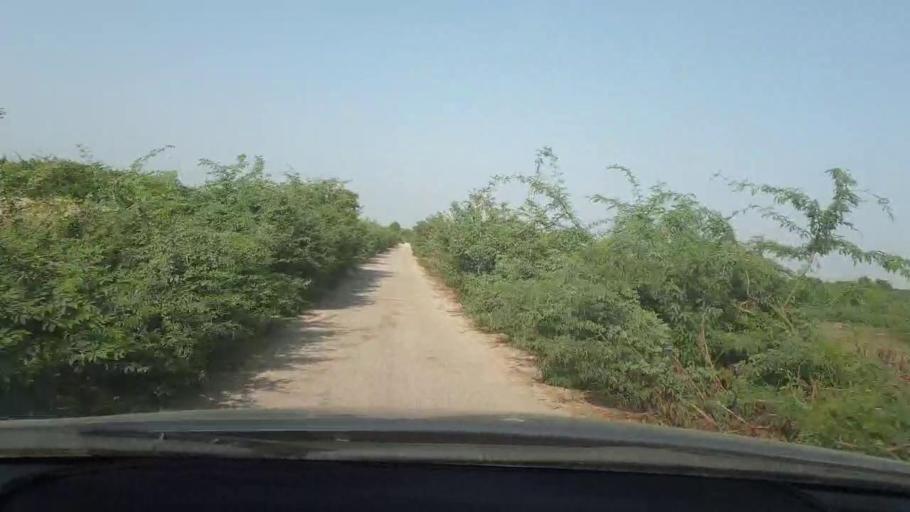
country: PK
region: Sindh
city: Naukot
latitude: 24.7754
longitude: 69.2601
